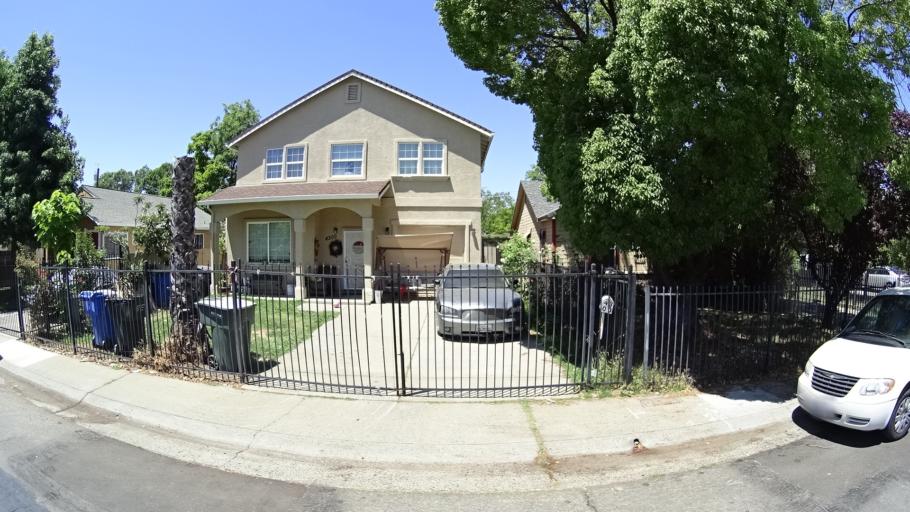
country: US
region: California
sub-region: Sacramento County
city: Parkway
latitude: 38.5362
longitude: -121.4682
